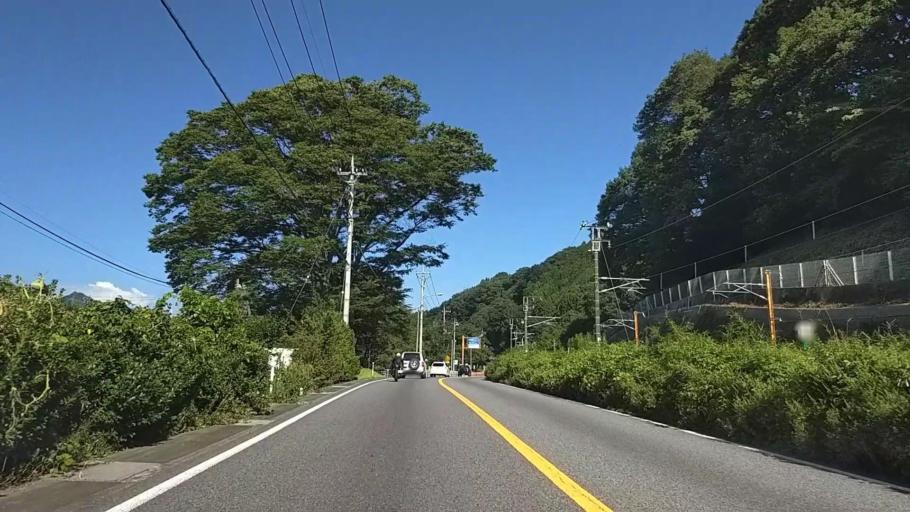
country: JP
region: Gunma
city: Annaka
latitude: 36.3304
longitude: 138.7523
